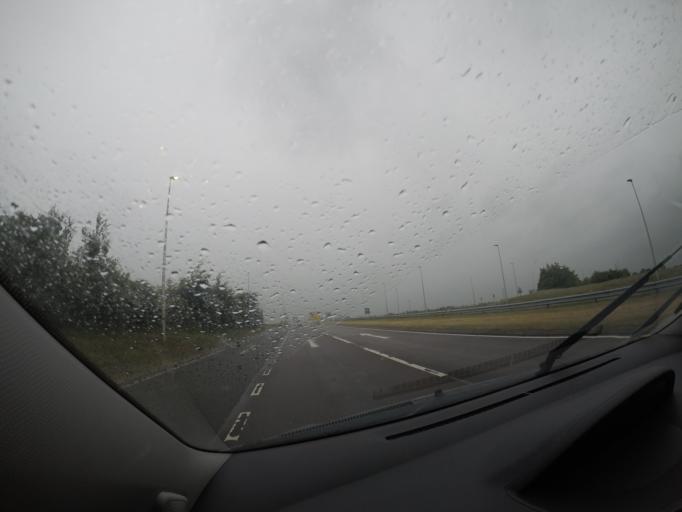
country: GB
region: Scotland
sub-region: Angus
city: Forfar
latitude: 56.6534
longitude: -2.9198
